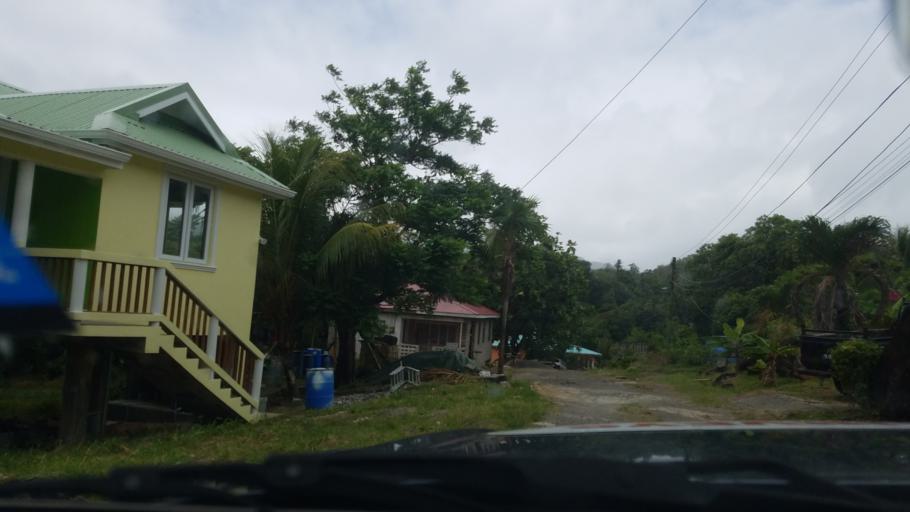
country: LC
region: Castries Quarter
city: Bisee
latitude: 14.0119
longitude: -60.9251
